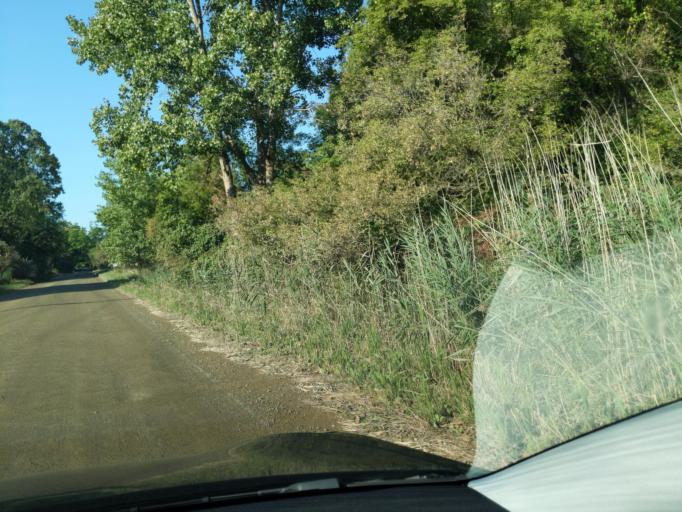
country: US
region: Michigan
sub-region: Oakland County
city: South Lyon
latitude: 42.4567
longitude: -83.6664
